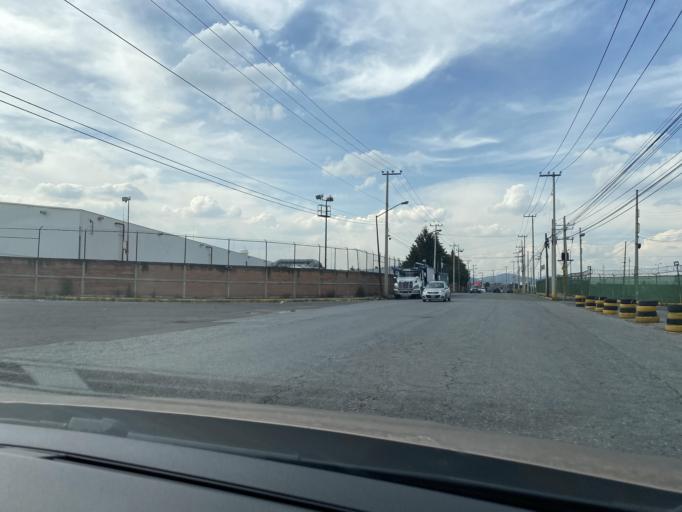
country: IN
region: Karnataka
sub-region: Dakshina Kannada
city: Puttur
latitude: 12.7511
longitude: 75.1961
